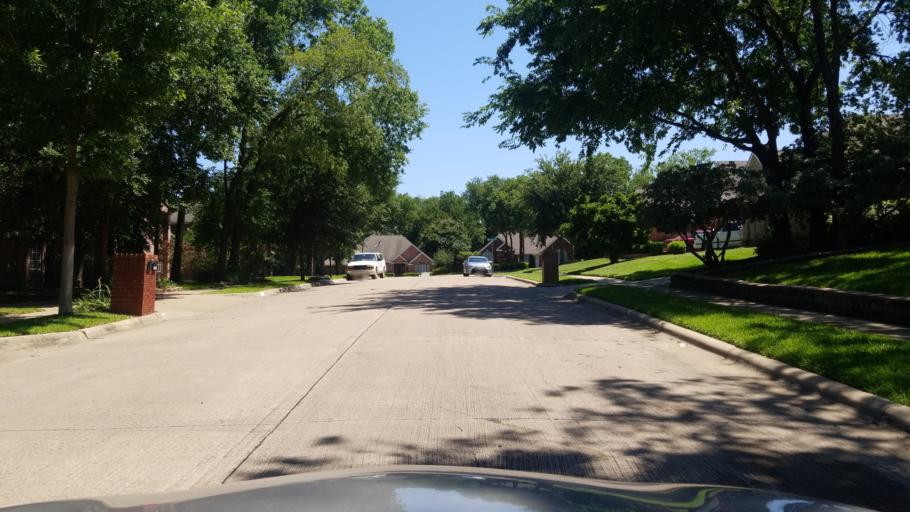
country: US
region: Texas
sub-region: Dallas County
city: Grand Prairie
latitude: 32.6892
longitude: -97.0025
